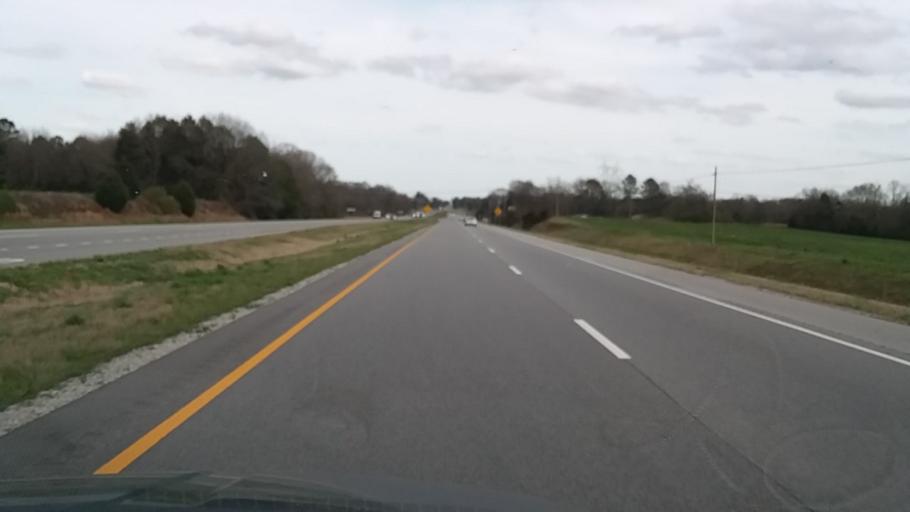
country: US
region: Alabama
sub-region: Lawrence County
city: Town Creek
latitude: 34.6824
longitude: -87.4581
